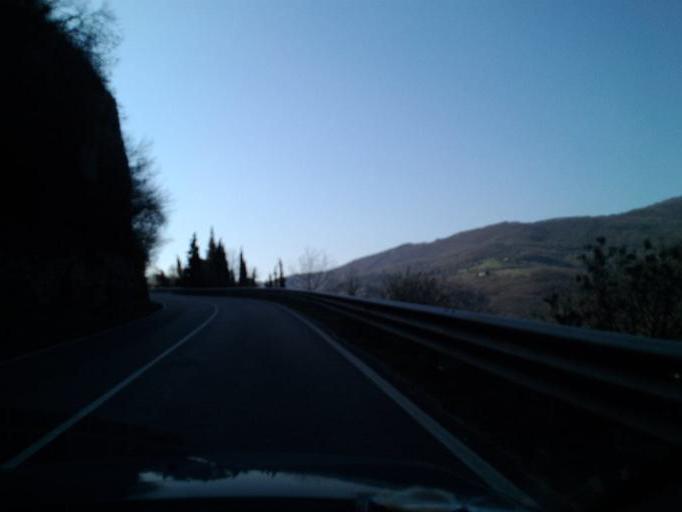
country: IT
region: Veneto
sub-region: Provincia di Verona
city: Stallavena-Lugo
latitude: 45.5493
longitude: 11.0050
